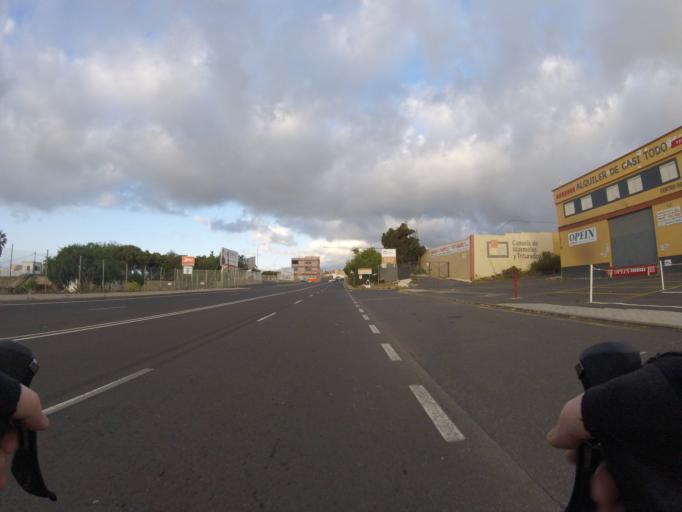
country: ES
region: Canary Islands
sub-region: Provincia de Santa Cruz de Tenerife
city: La Laguna
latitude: 28.4260
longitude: -16.3156
